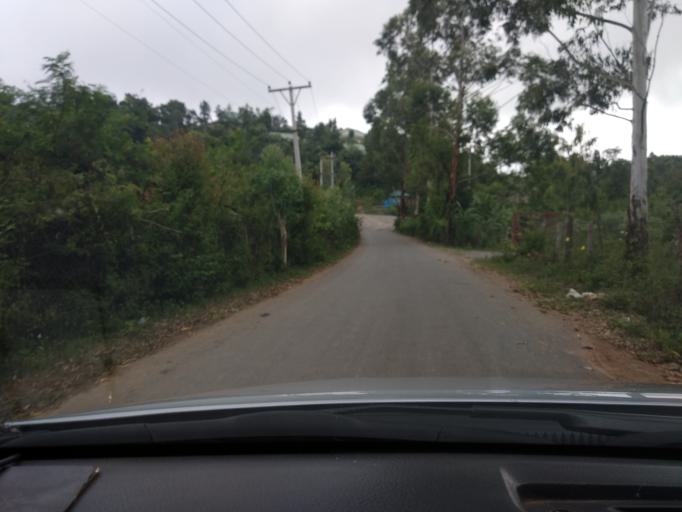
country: MM
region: Mandalay
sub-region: Pyin Oo Lwin District
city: Pyin Oo Lwin
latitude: 21.9148
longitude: 96.3833
